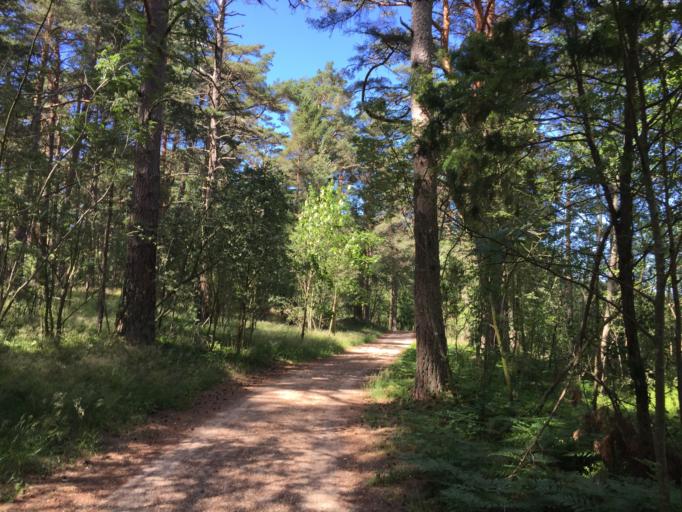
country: LV
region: Ventspils
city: Ventspils
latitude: 57.4478
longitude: 21.6296
